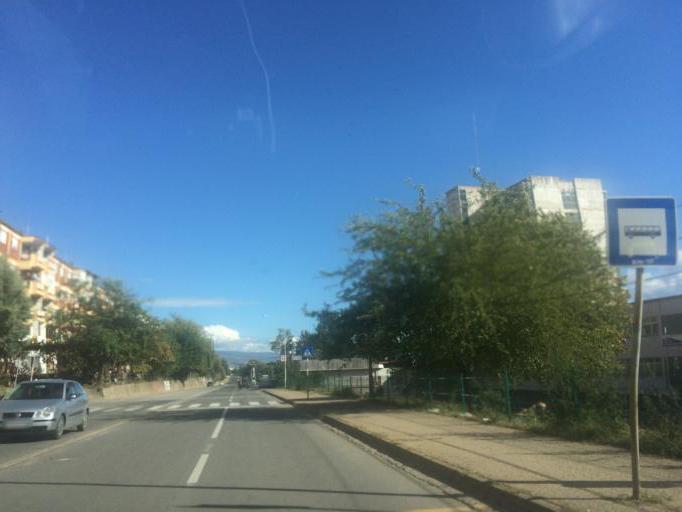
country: MK
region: Kocani
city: Kochani
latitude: 41.9142
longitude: 22.4260
